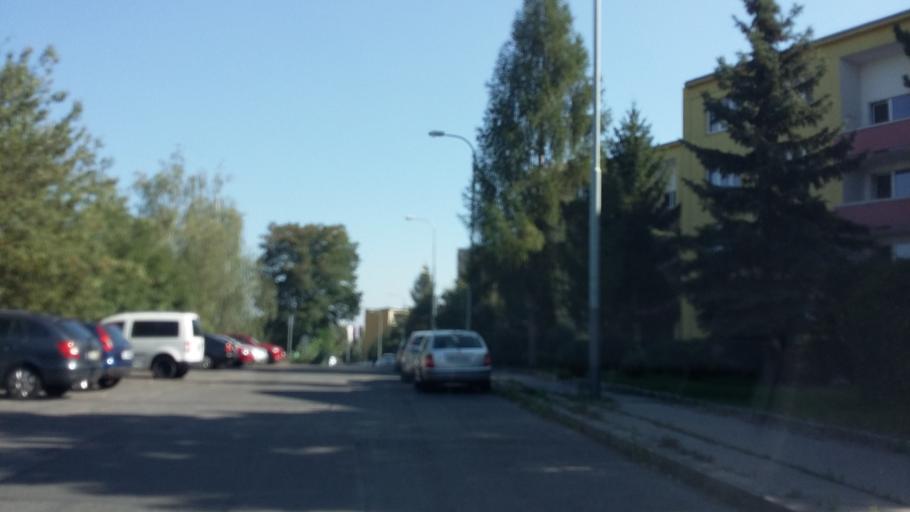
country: CZ
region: Praha
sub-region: Praha 9
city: Vysocany
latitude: 50.0574
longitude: 14.5173
